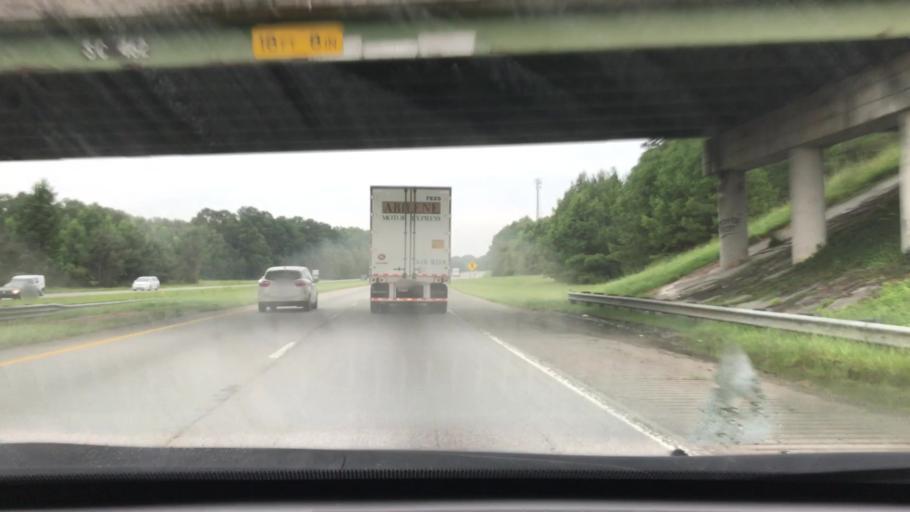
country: US
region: South Carolina
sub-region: Jasper County
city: Ridgeland
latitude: 32.5796
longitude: -80.9304
